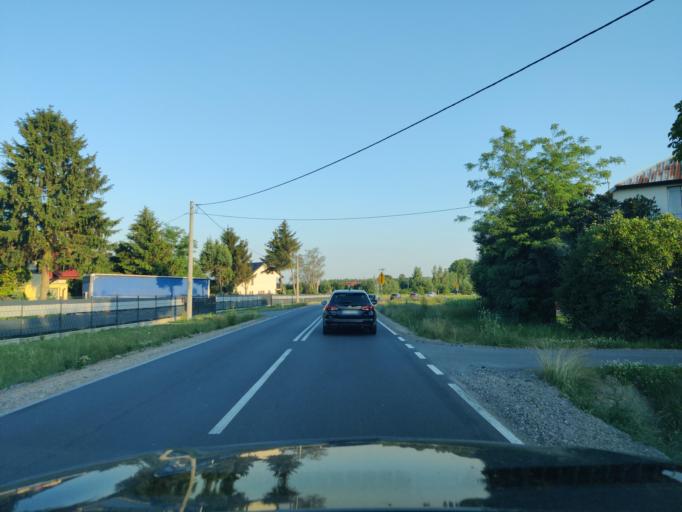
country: PL
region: Masovian Voivodeship
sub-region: Powiat plonski
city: Baboszewo
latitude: 52.7085
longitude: 20.3381
